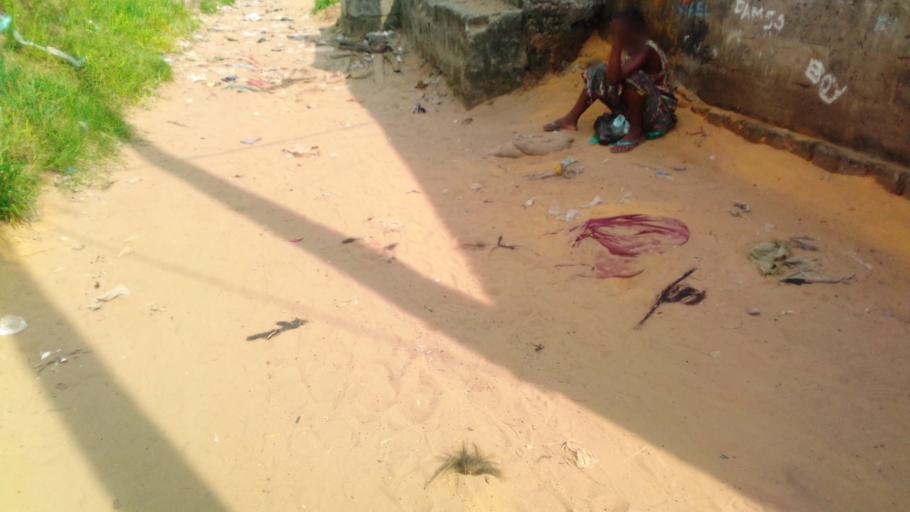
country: CD
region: Kinshasa
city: Masina
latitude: -4.3979
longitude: 15.3444
